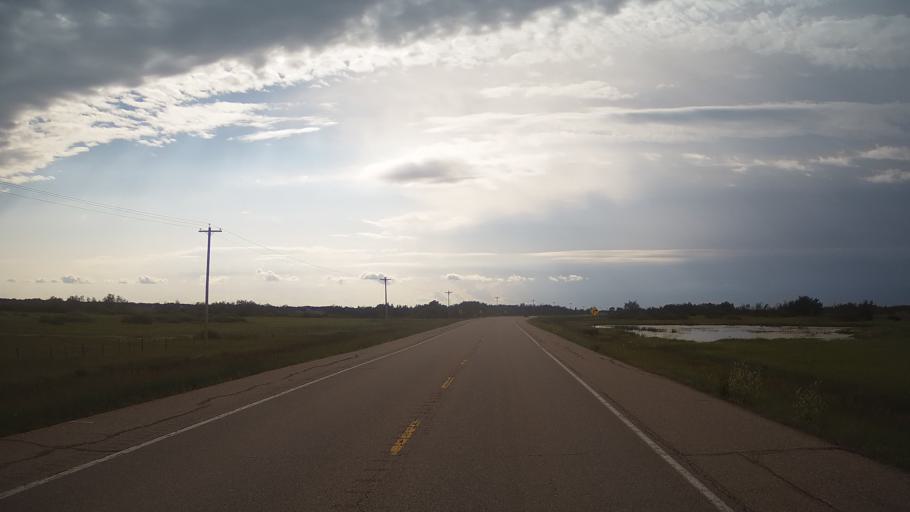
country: CA
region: Alberta
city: Viking
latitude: 53.1313
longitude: -111.9080
